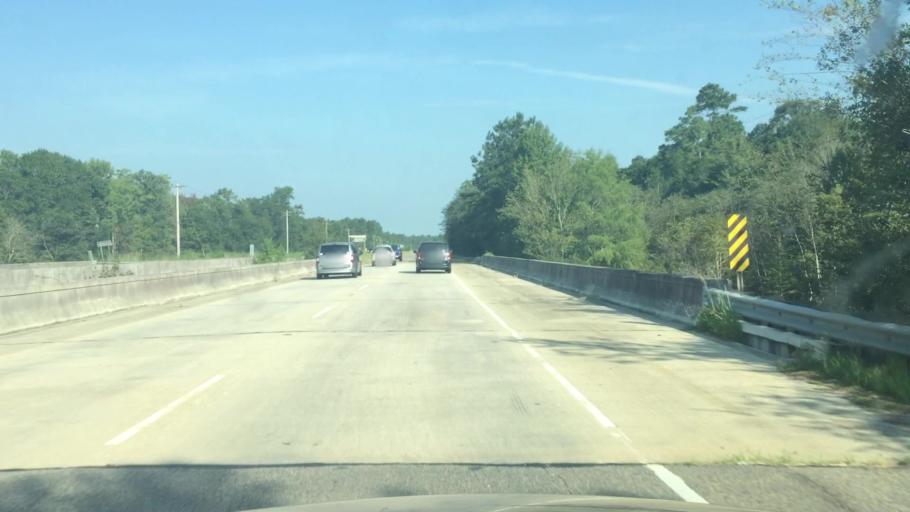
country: US
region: South Carolina
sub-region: Horry County
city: North Myrtle Beach
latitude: 33.9089
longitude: -78.7098
